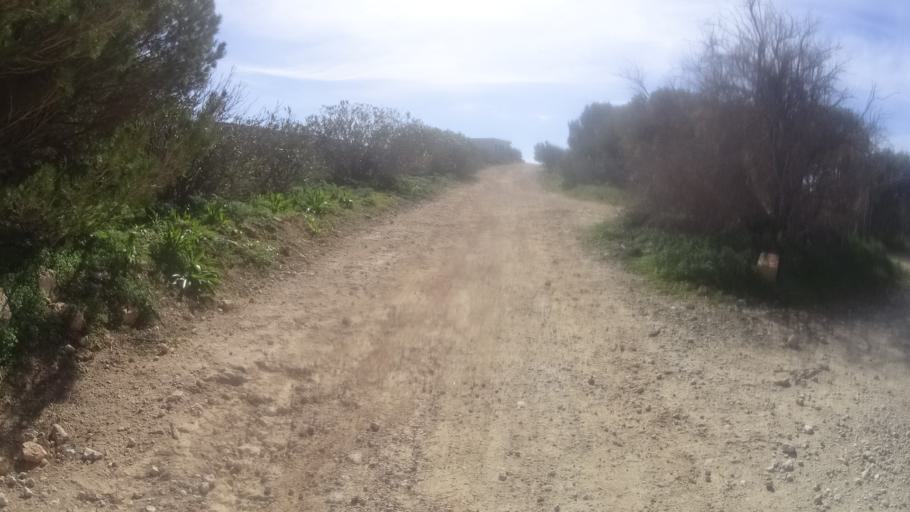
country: MT
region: Il-Qala
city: Qala
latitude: 36.0123
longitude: 14.3326
